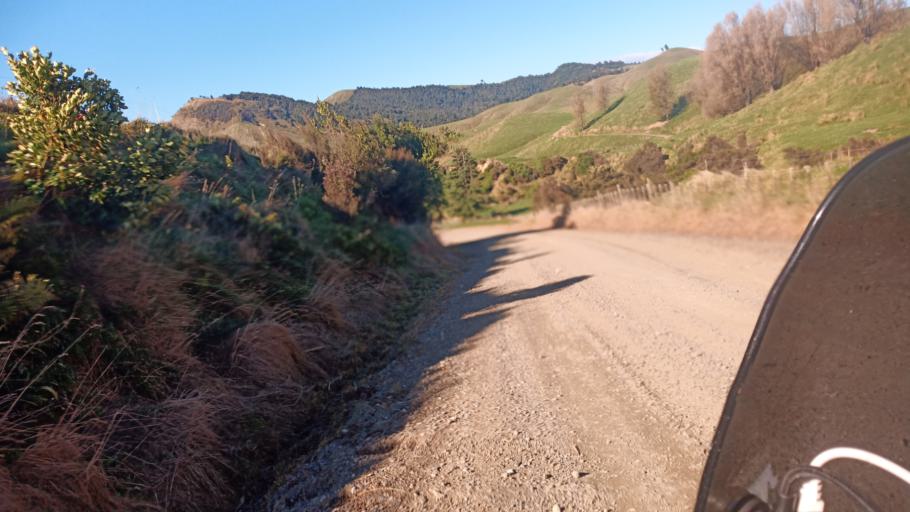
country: NZ
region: Hawke's Bay
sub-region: Wairoa District
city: Wairoa
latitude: -38.7399
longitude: 177.2897
